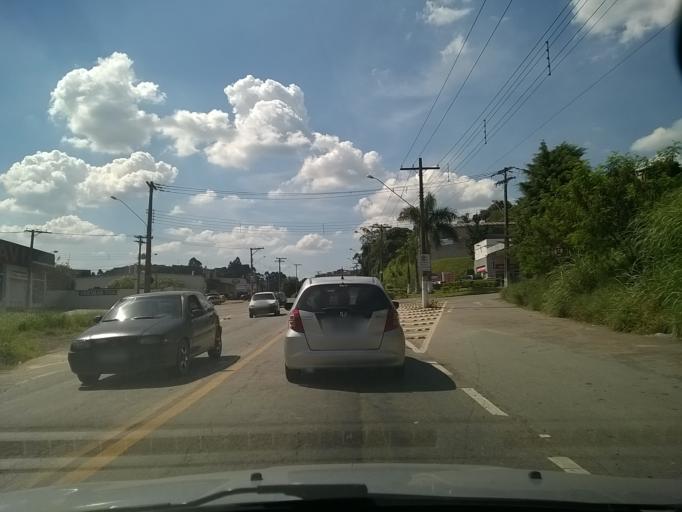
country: BR
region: Sao Paulo
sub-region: Francisco Morato
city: Francisco Morato
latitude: -23.2943
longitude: -46.7531
